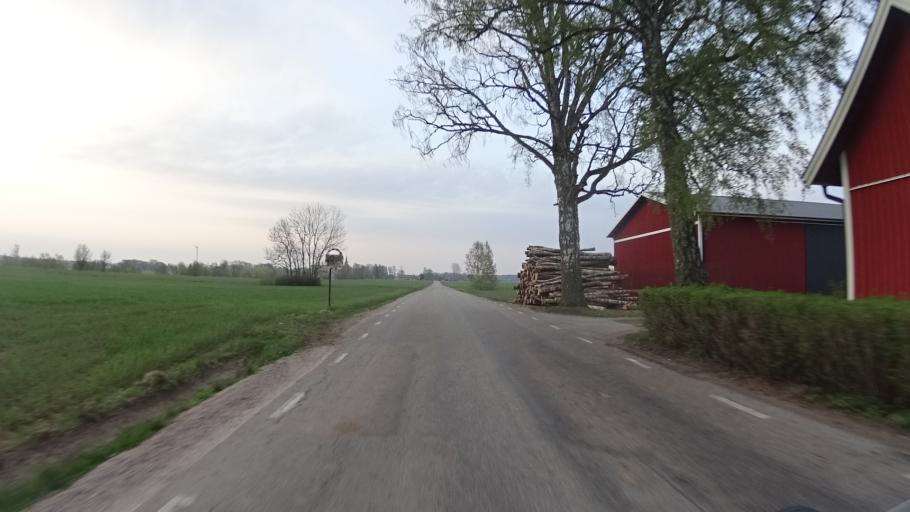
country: SE
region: Vaestra Goetaland
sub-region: Gotene Kommun
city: Kallby
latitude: 58.4796
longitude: 13.3195
